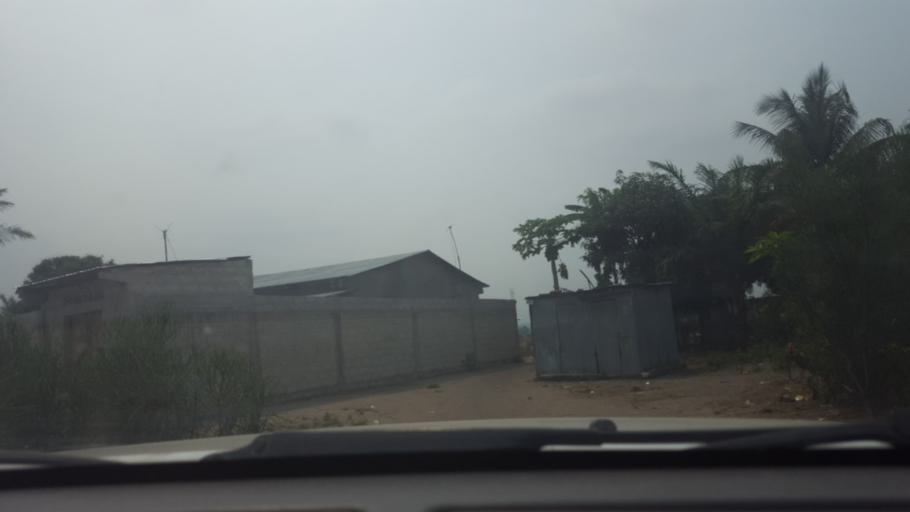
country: CD
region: Kinshasa
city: Masina
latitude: -4.3609
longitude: 15.5123
